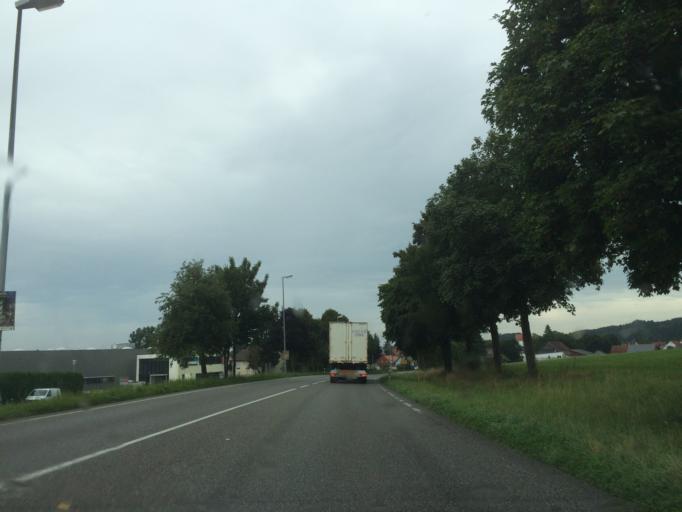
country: DE
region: Baden-Wuerttemberg
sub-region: Tuebingen Region
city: Bad Waldsee
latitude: 47.8920
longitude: 9.7170
